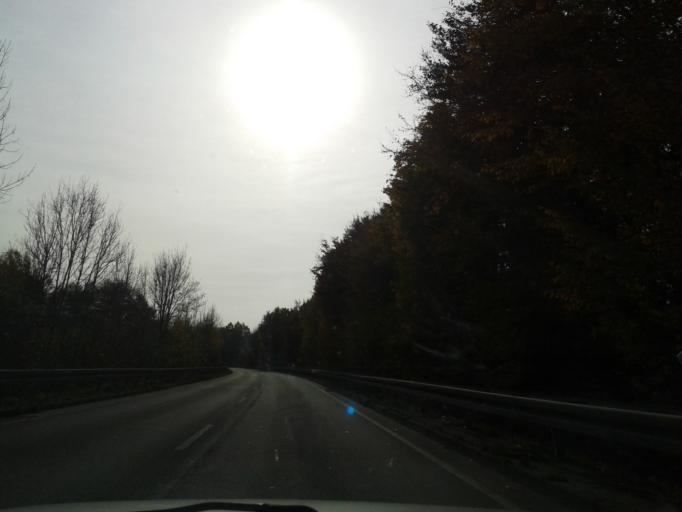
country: DE
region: North Rhine-Westphalia
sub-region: Regierungsbezirk Arnsberg
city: Ruthen
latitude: 51.4520
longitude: 8.4365
